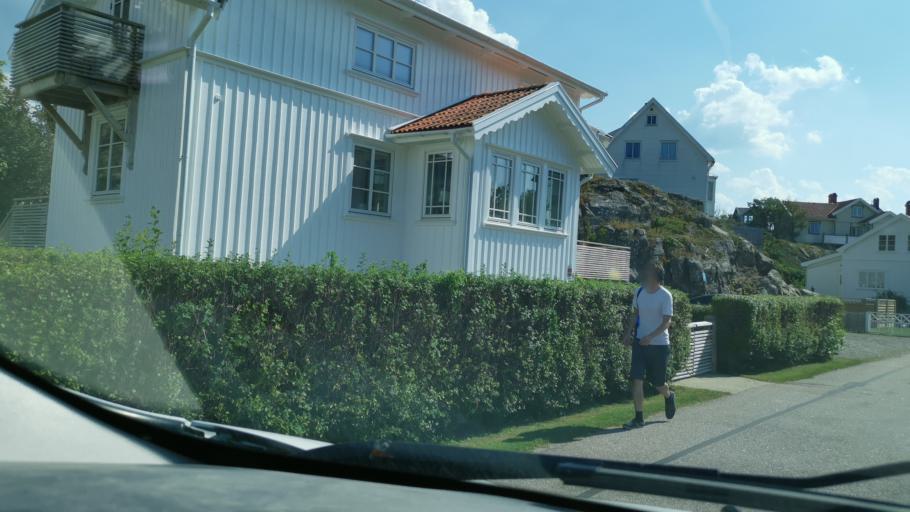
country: SE
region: Vaestra Goetaland
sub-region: Lysekils Kommun
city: Lysekil
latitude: 58.2141
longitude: 11.4200
